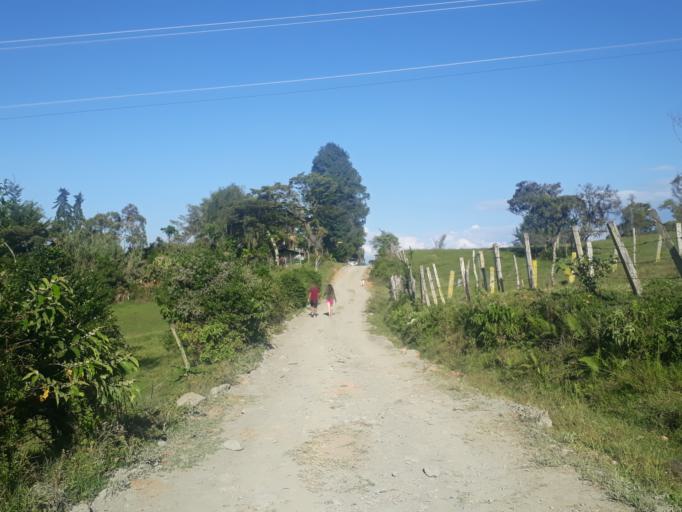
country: CO
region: Santander
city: Velez
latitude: 6.0290
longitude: -73.6684
